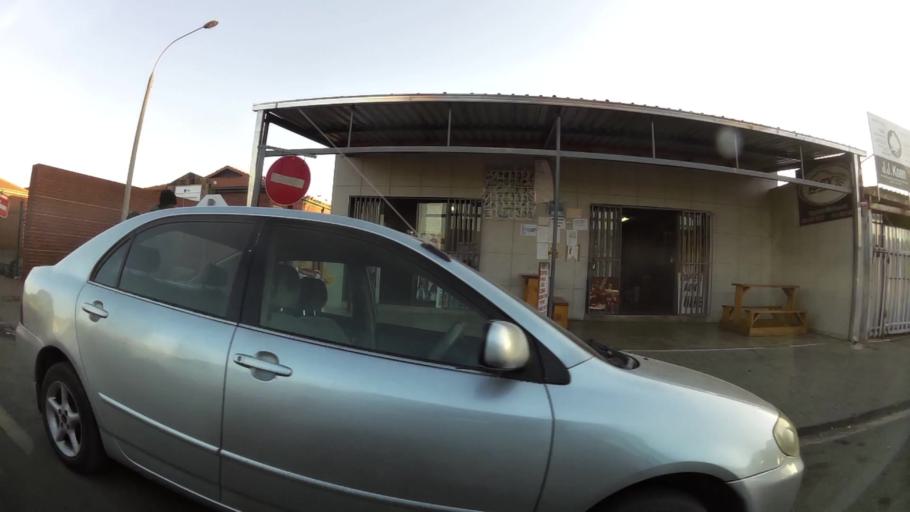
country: ZA
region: North-West
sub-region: Bojanala Platinum District Municipality
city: Rustenburg
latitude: -25.6687
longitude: 27.2476
